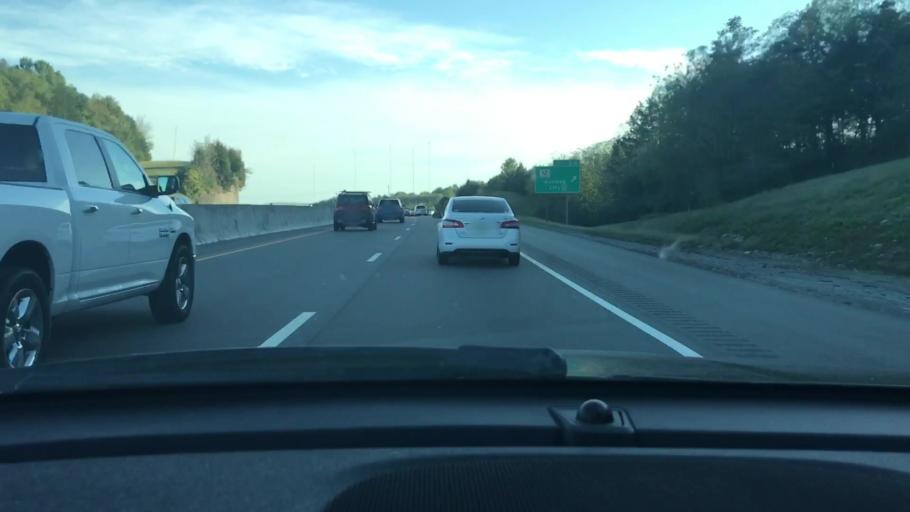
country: US
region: Tennessee
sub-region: Davidson County
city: Nashville
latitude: 36.2143
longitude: -86.8724
